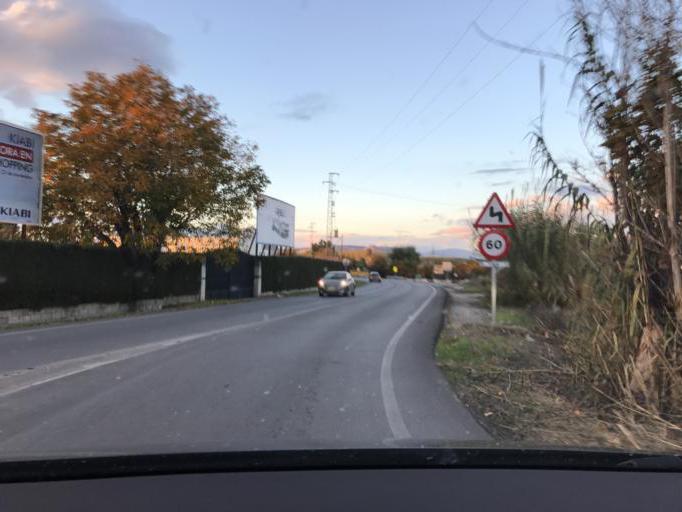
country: ES
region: Andalusia
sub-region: Provincia de Granada
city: Cullar-Vega
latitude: 37.1800
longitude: -3.6716
